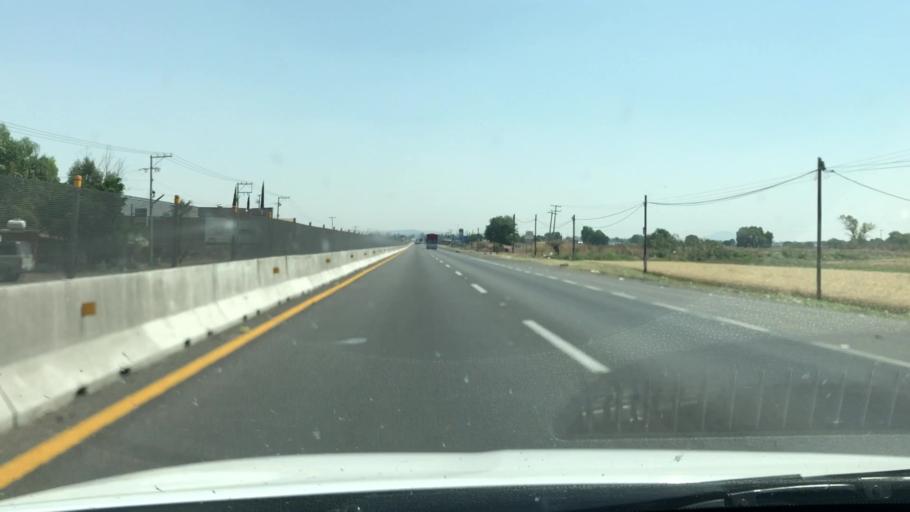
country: MX
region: Guanajuato
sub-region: Abasolo
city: San Bernardo Pena Blanca
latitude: 20.4706
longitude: -101.5043
